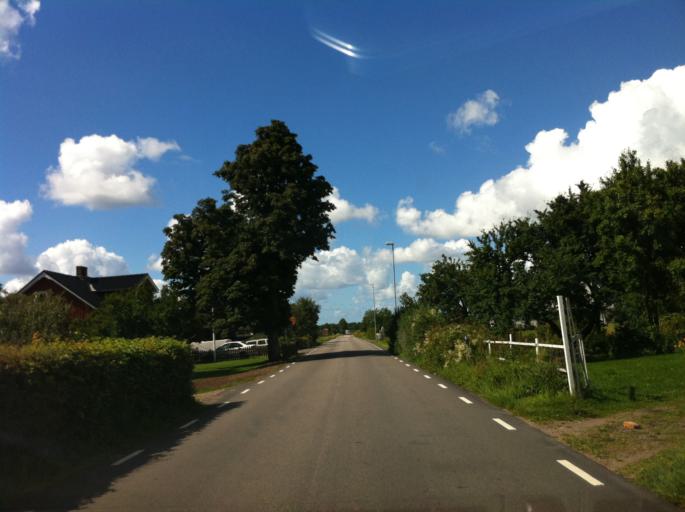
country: SE
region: Skane
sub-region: Angelholms Kommun
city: AEngelholm
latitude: 56.2457
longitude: 12.8724
